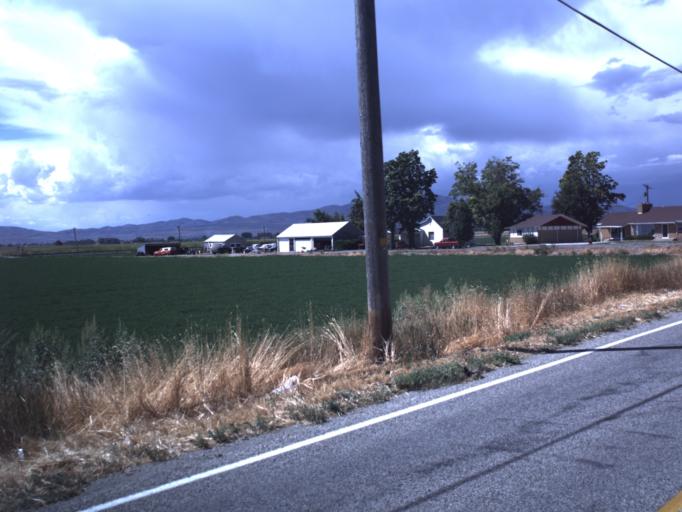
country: US
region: Utah
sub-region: Box Elder County
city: Honeyville
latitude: 41.6629
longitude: -112.0881
